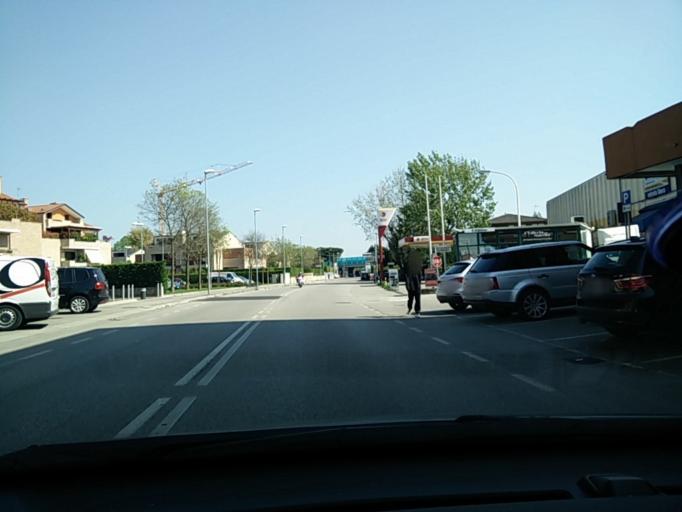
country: IT
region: Veneto
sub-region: Provincia di Padova
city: Noventa
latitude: 45.4217
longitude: 11.9445
